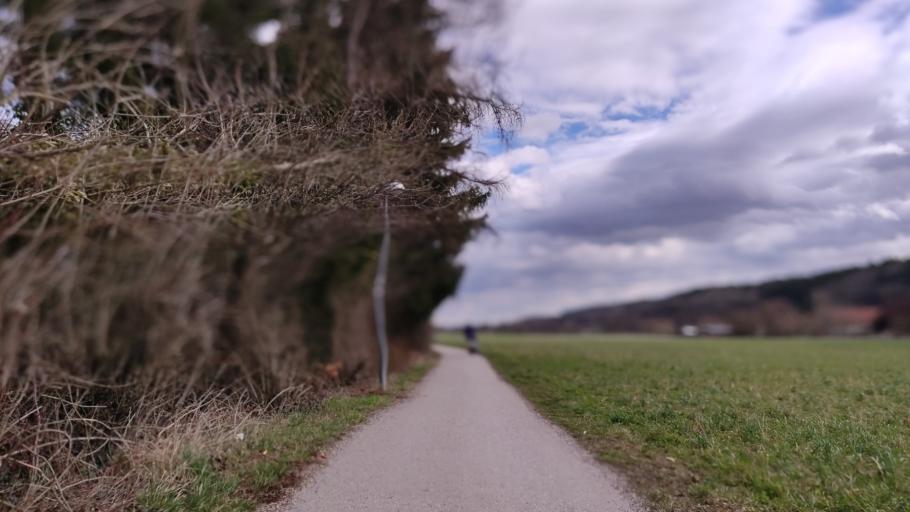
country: DE
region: Bavaria
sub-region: Upper Bavaria
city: Emmering
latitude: 48.1754
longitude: 11.2716
